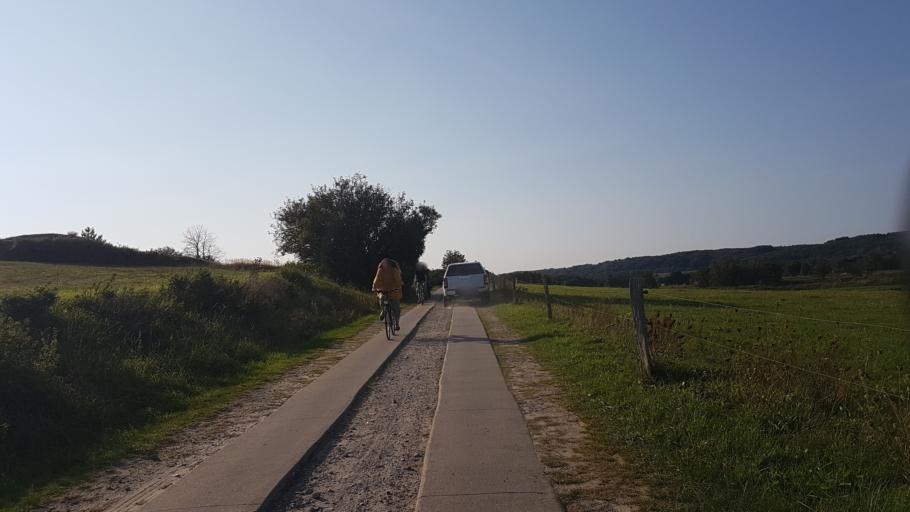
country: DE
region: Mecklenburg-Vorpommern
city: Ostseebad Sellin
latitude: 54.3562
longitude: 13.6468
